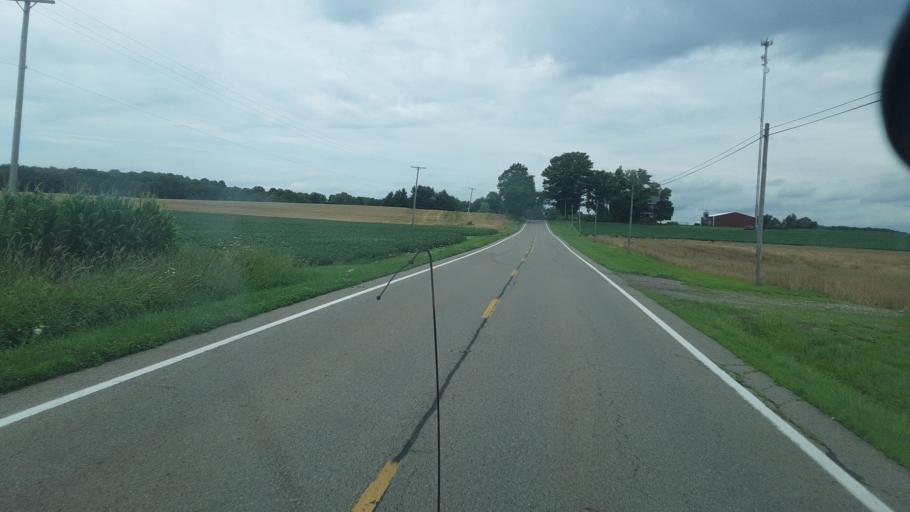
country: US
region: Ohio
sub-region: Trumbull County
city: Cortland
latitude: 41.4382
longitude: -80.6655
